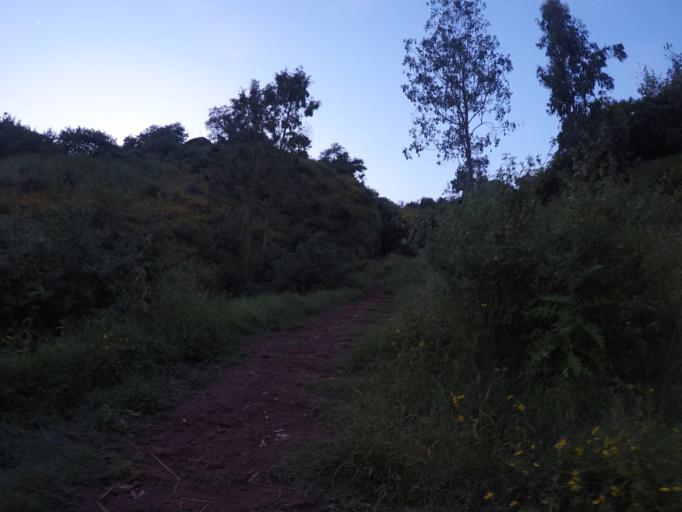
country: ET
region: Amhara
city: Lalibela
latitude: 12.0316
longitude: 39.0466
